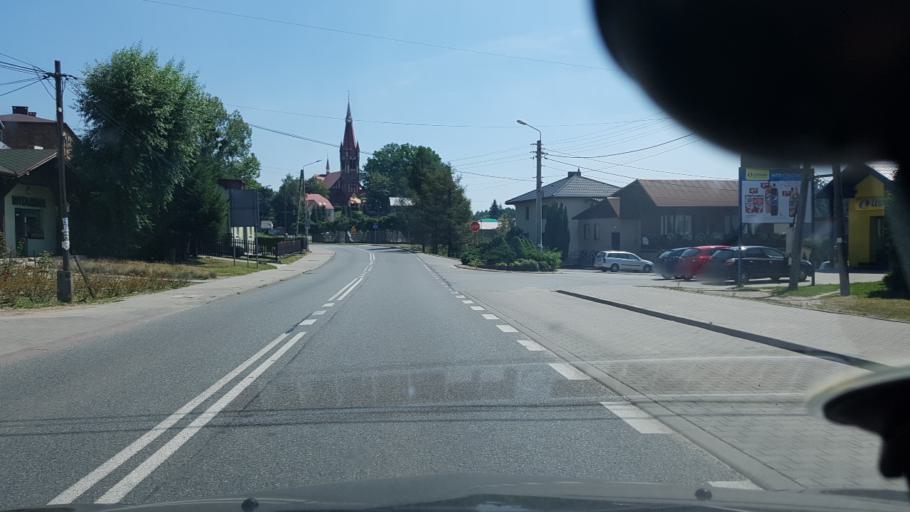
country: PL
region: Silesian Voivodeship
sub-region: Powiat wodzislawski
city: Marklowice
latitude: 50.0183
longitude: 18.5139
